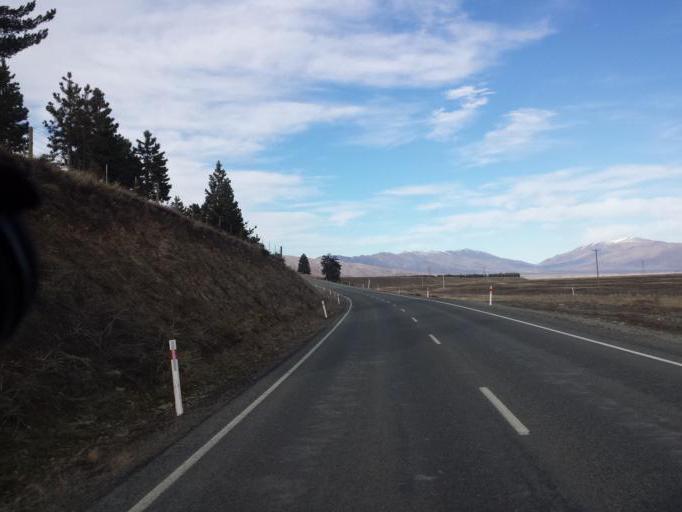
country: NZ
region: Canterbury
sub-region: Timaru District
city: Pleasant Point
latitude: -44.0639
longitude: 170.5043
